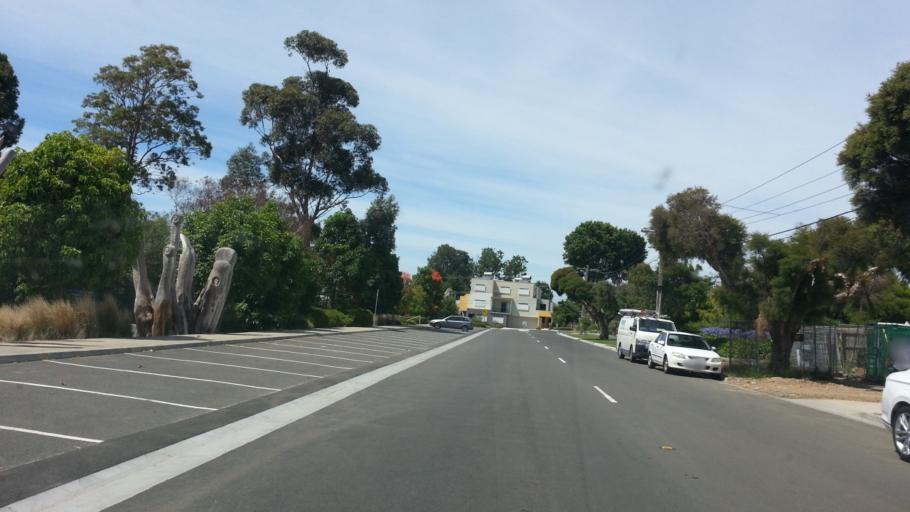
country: AU
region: Victoria
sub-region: Knox
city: Boronia
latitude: -37.8637
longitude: 145.2829
